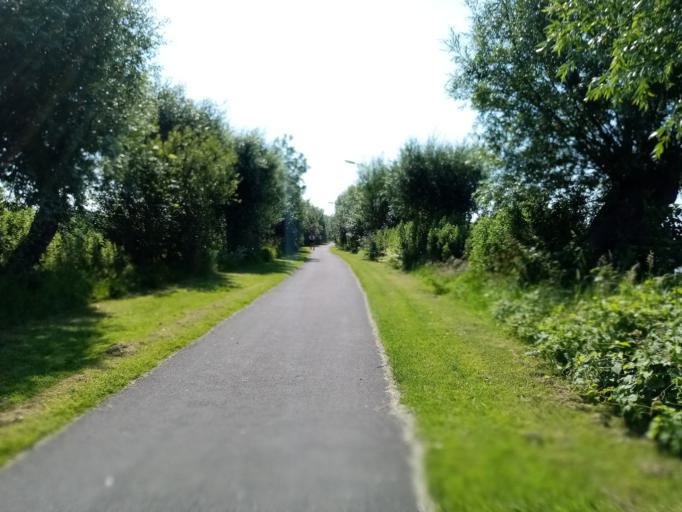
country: NL
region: South Holland
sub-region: Gemeente Kaag en Braassem
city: Leimuiden
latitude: 52.1900
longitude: 4.7168
